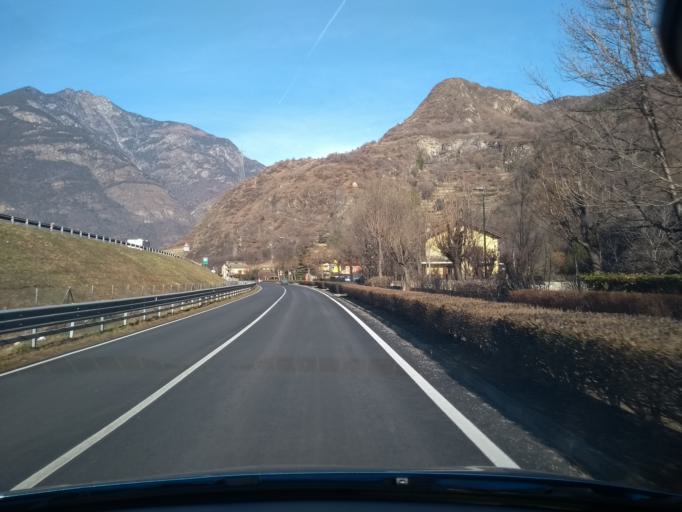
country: IT
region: Aosta Valley
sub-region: Valle d'Aosta
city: Verres
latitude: 45.6741
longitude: 7.6819
